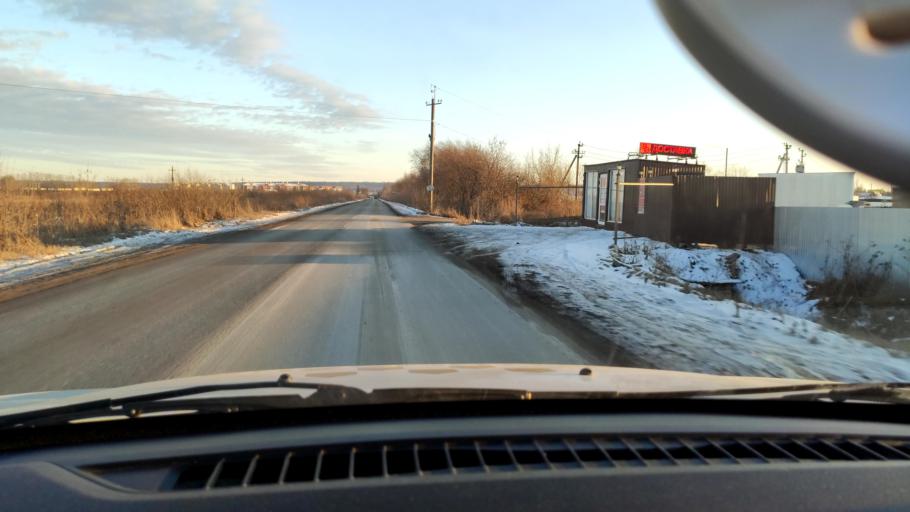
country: RU
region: Perm
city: Ferma
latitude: 57.9024
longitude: 56.2855
